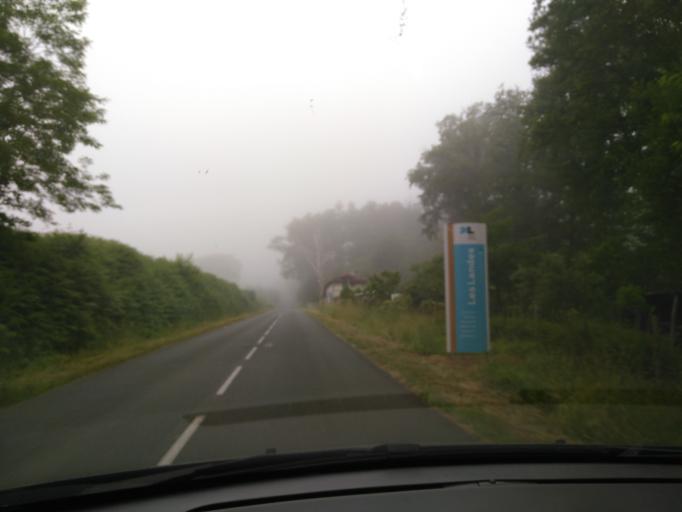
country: FR
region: Midi-Pyrenees
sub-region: Departement du Gers
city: Le Houga
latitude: 43.8604
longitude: -0.2049
